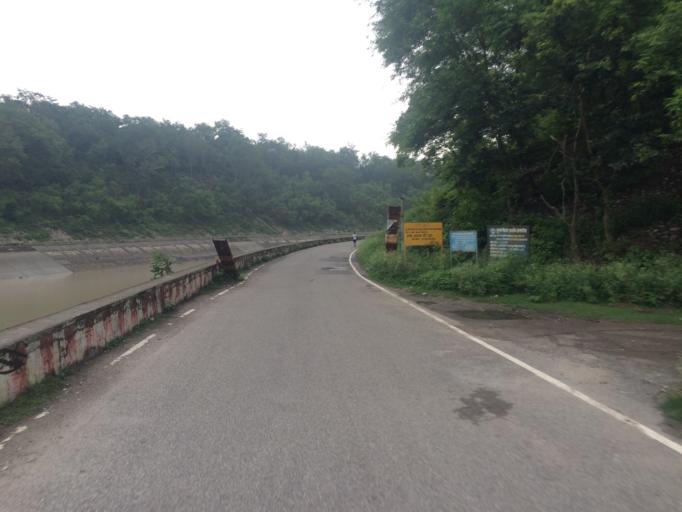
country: IN
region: Uttarakhand
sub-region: Dehradun
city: Birbhaddar
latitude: 30.0723
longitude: 78.2917
